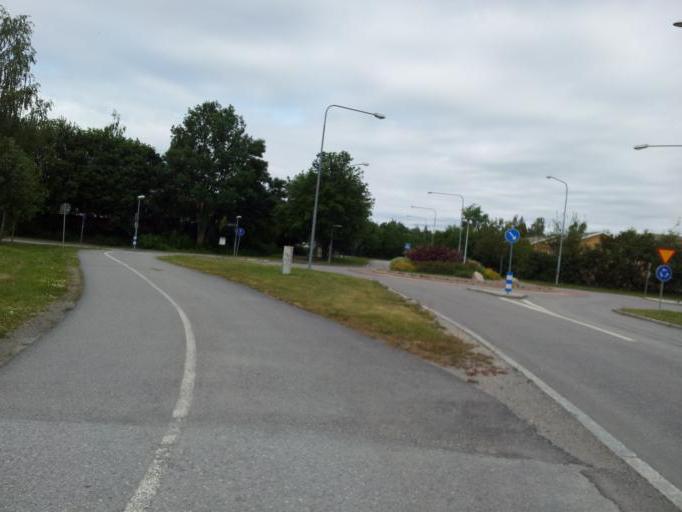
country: SE
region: Uppsala
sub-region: Uppsala Kommun
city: Gamla Uppsala
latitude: 59.8832
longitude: 17.6451
